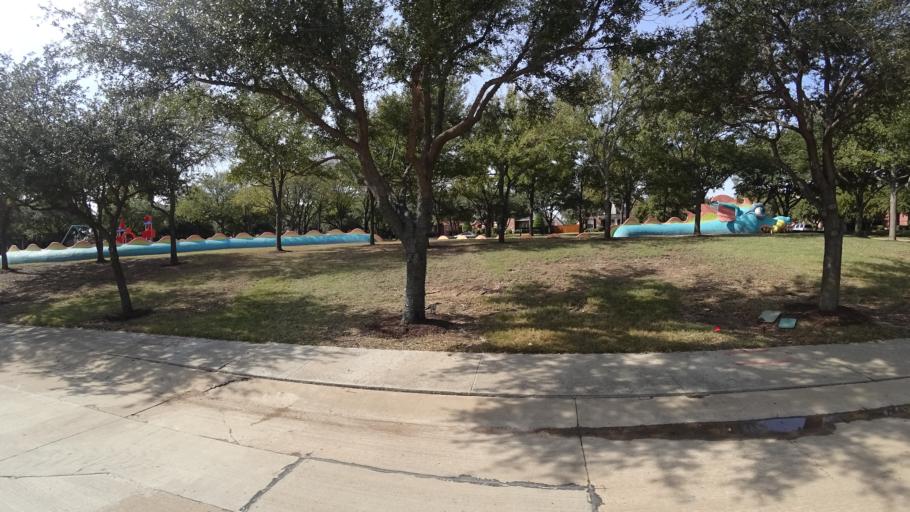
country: US
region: Texas
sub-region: Denton County
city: The Colony
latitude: 33.0353
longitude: -96.8888
